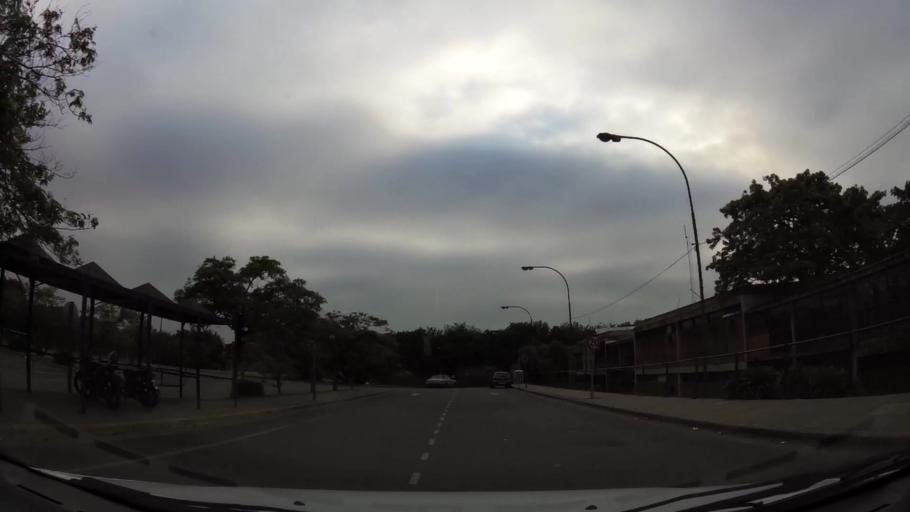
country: AR
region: Buenos Aires
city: San Justo
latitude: -34.6959
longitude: -58.5791
